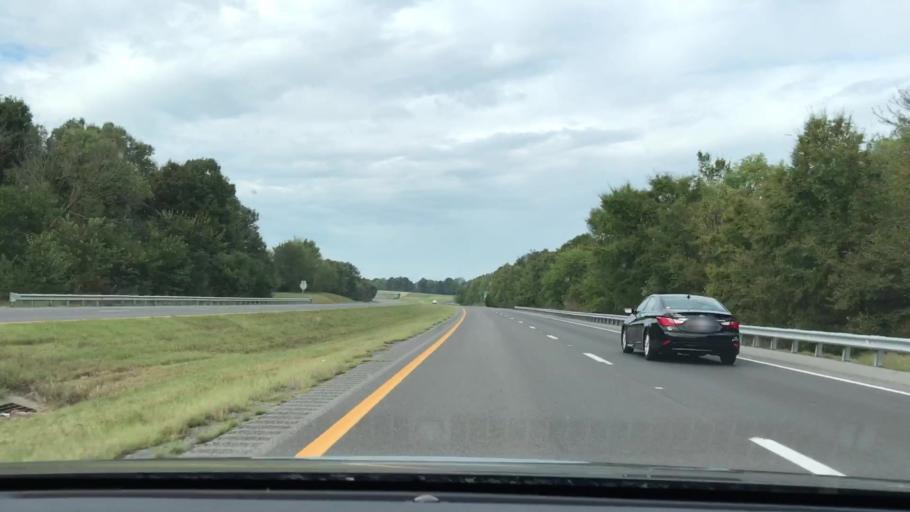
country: US
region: Kentucky
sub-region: Graves County
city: Mayfield
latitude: 36.7775
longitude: -88.5868
